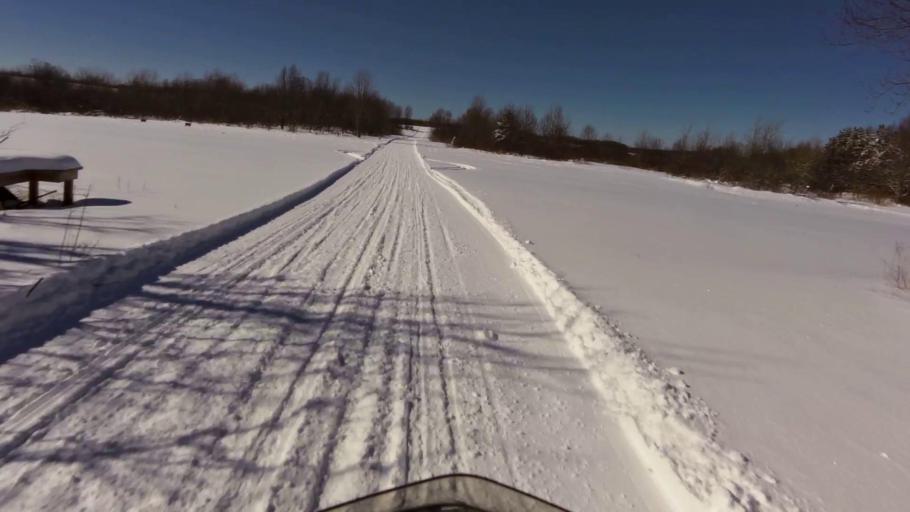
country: US
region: New York
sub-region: Chautauqua County
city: Lakewood
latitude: 42.2257
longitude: -79.3305
